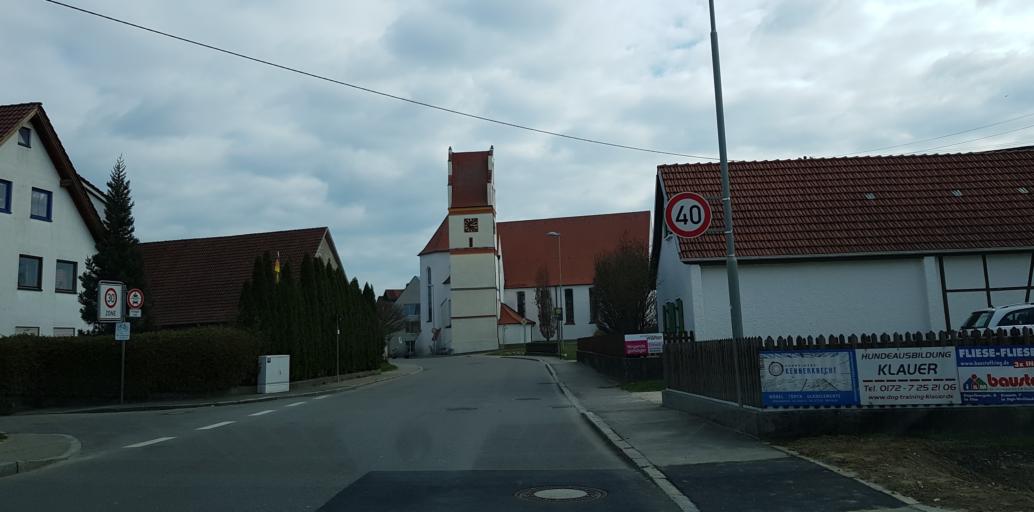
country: DE
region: Baden-Wuerttemberg
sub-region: Tuebingen Region
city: Erbach
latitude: 48.3544
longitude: 9.8949
